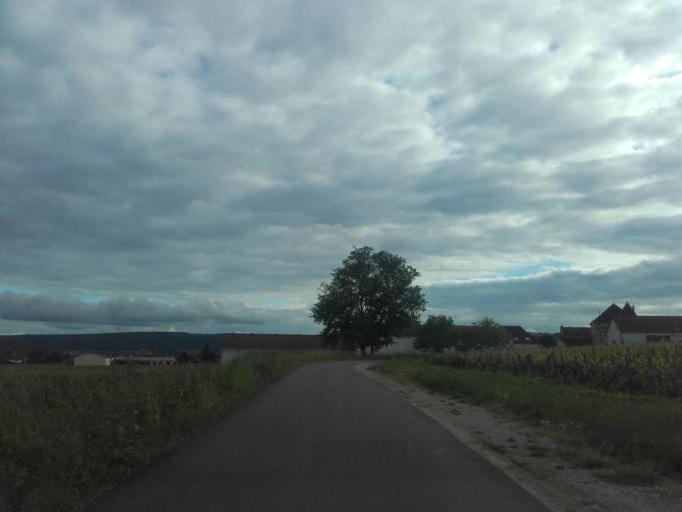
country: FR
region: Bourgogne
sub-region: Departement de Saone-et-Loire
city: Mellecey
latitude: 46.8417
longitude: 4.7383
